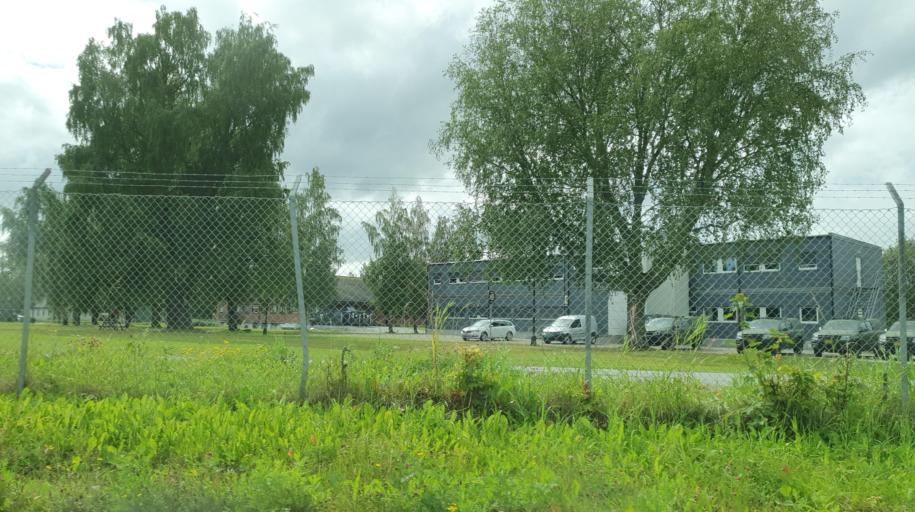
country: NO
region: Nord-Trondelag
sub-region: Stjordal
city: Stjordalshalsen
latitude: 63.4637
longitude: 10.9419
